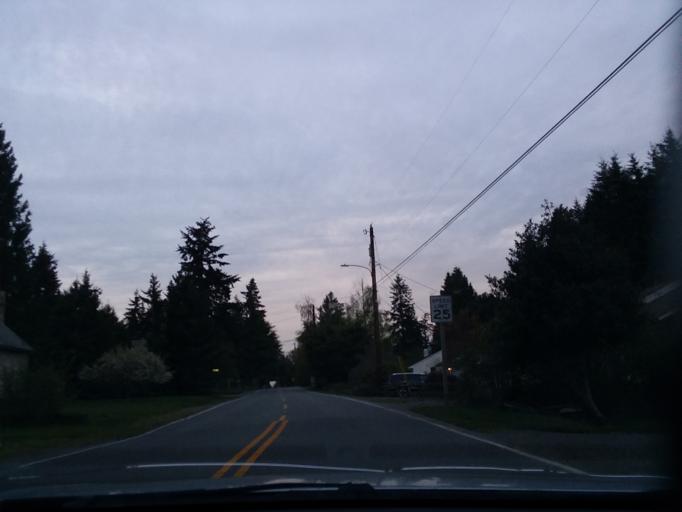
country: US
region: Washington
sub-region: Snohomish County
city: Esperance
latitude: 47.7998
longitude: -122.3410
